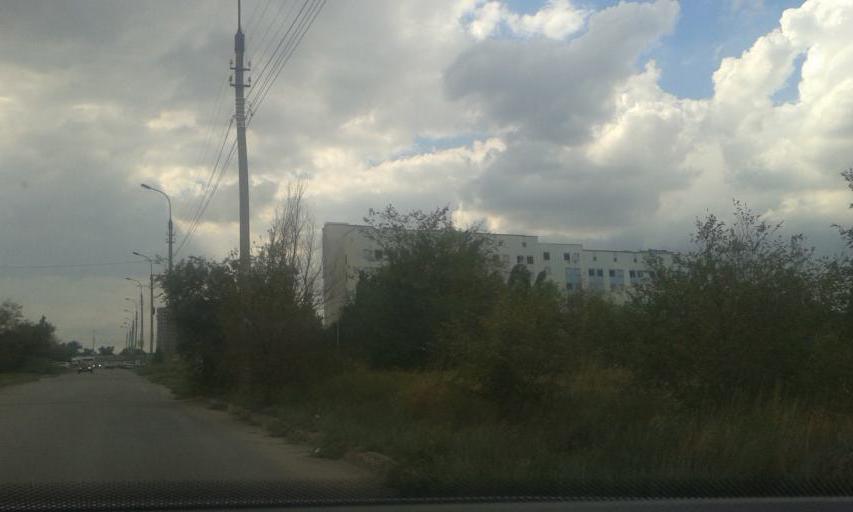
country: RU
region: Volgograd
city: Volgograd
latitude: 48.6415
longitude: 44.4191
